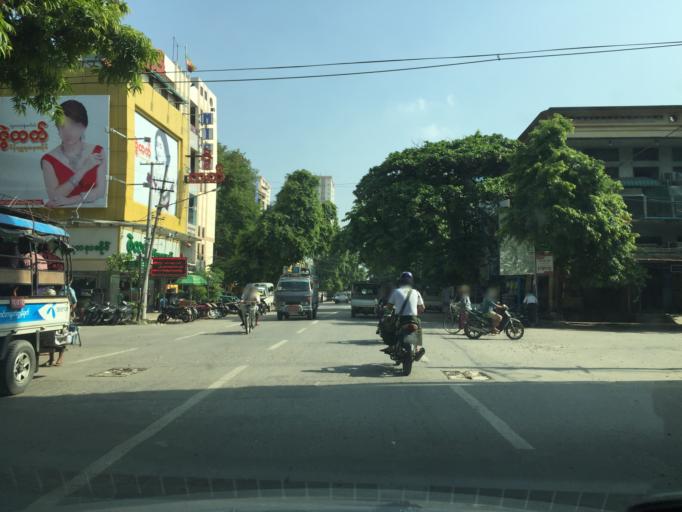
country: MM
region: Mandalay
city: Mandalay
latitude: 21.9772
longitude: 96.0775
